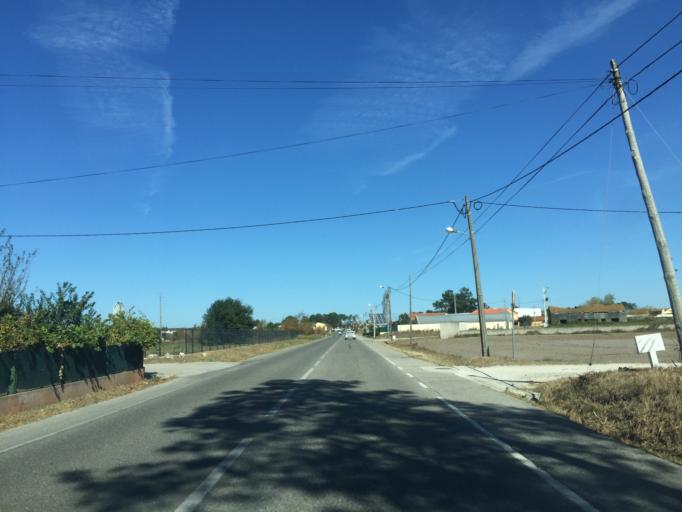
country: PT
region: Coimbra
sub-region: Figueira da Foz
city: Alhadas
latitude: 40.2522
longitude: -8.7835
